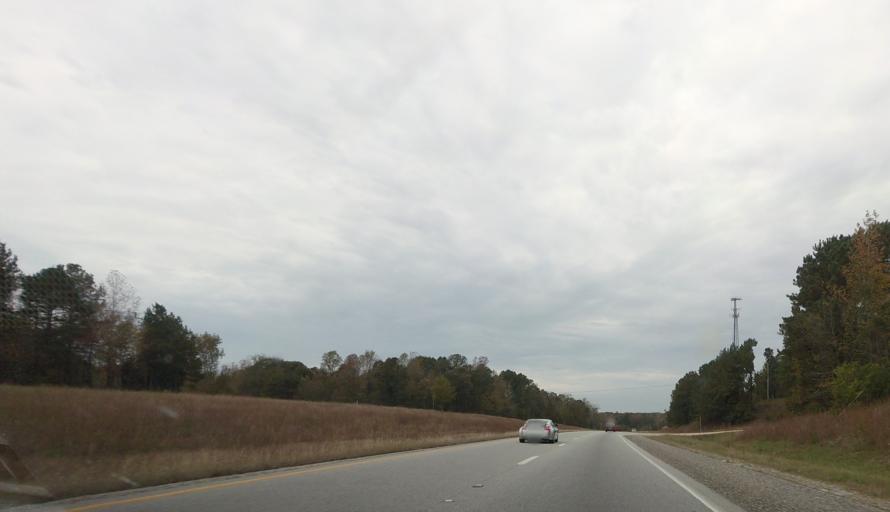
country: US
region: Alabama
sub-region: Lee County
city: Opelika
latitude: 32.6385
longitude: -85.3099
